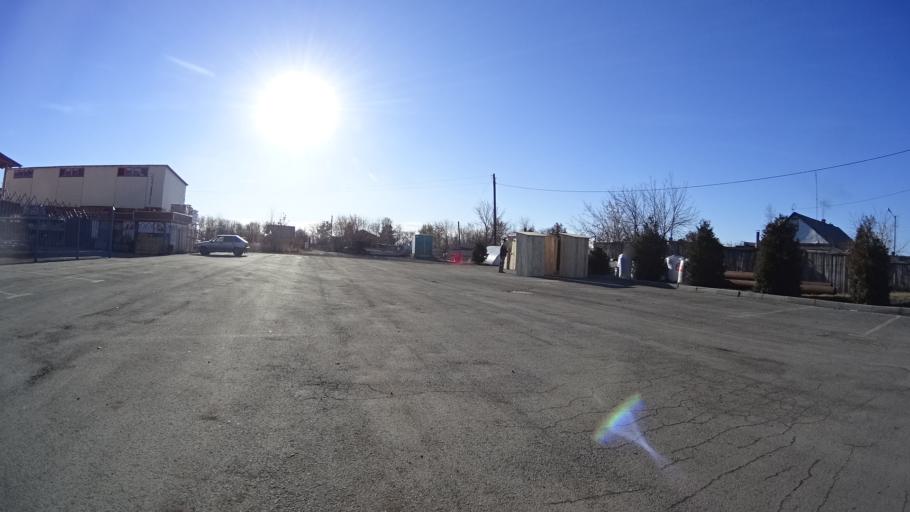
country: RU
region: Chelyabinsk
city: Troitsk
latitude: 54.0832
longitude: 61.5107
